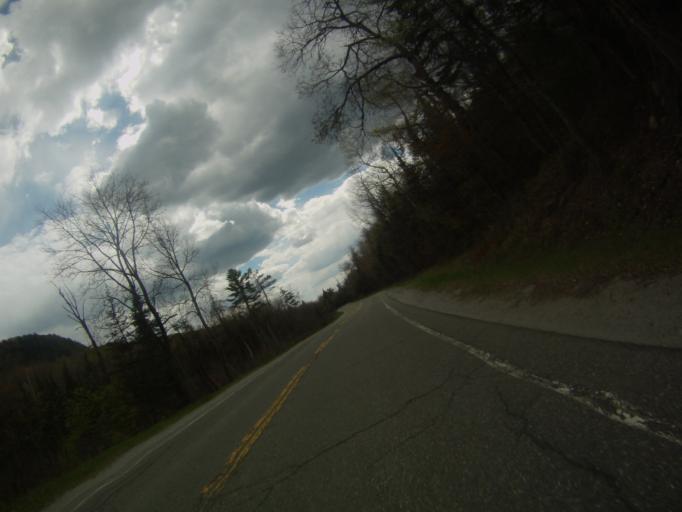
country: US
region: New York
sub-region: Essex County
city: Mineville
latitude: 44.0959
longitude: -73.5736
